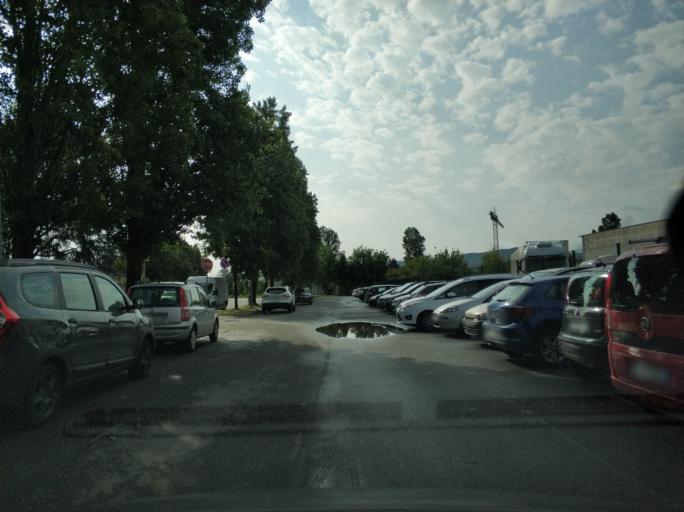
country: IT
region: Piedmont
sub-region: Provincia di Torino
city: Settimo Torinese
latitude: 45.1225
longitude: 7.7536
